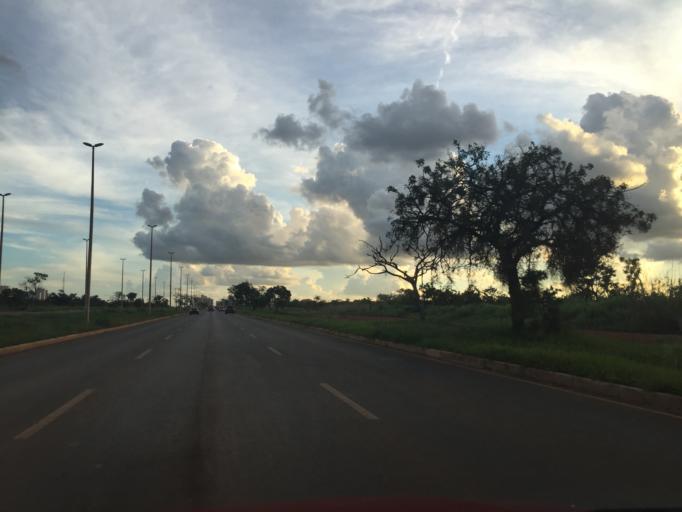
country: BR
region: Federal District
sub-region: Brasilia
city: Brasilia
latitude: -15.8036
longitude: -47.9919
